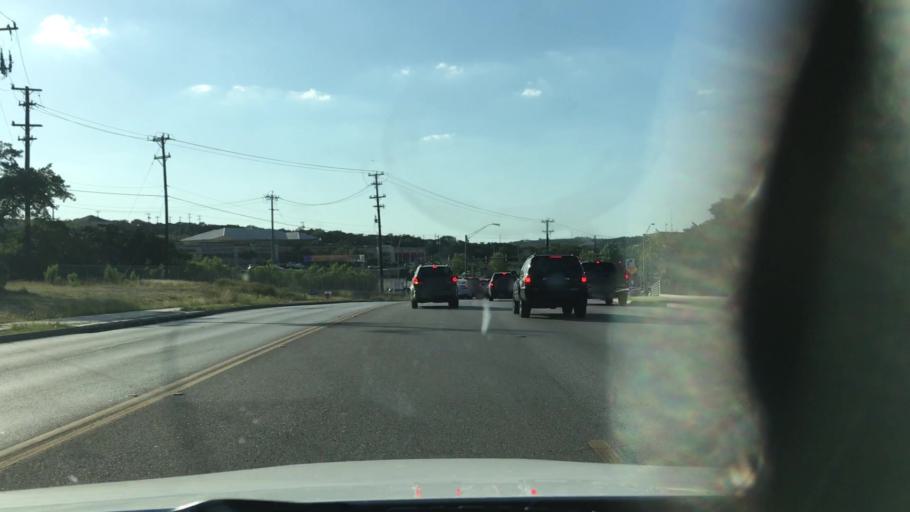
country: US
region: Texas
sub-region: Bexar County
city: Timberwood Park
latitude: 29.6600
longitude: -98.4341
